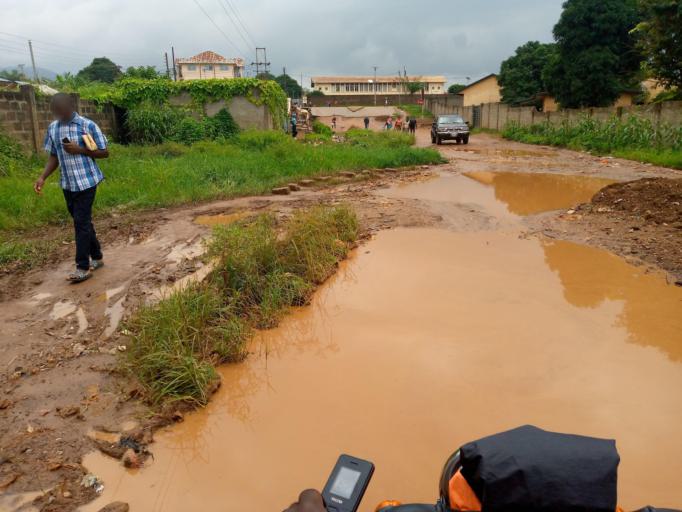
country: SL
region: Eastern Province
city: Kenema
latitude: 7.8745
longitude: -11.1832
